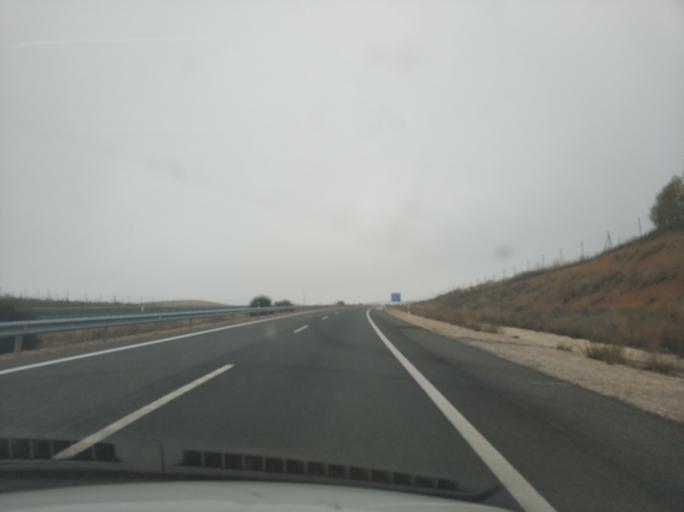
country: ES
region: Castille and Leon
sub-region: Provincia de Soria
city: Adradas
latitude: 41.3636
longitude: -2.4702
